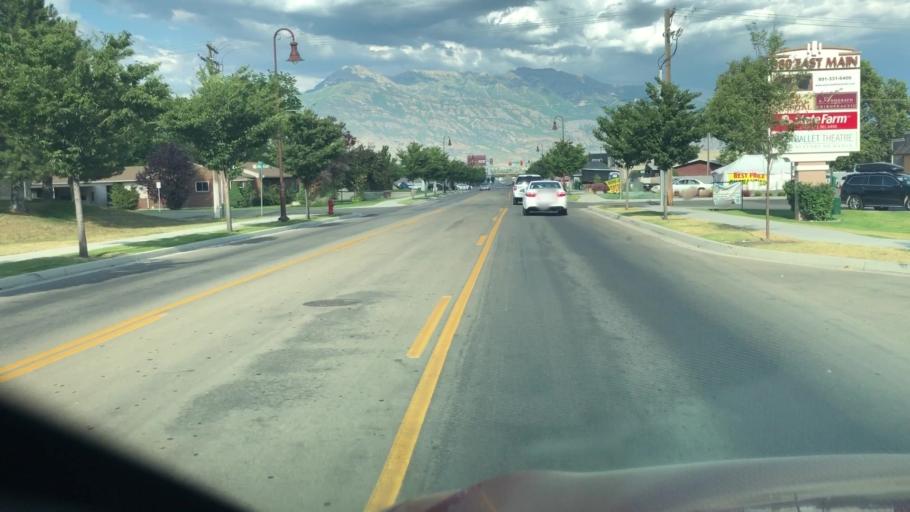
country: US
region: Utah
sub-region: Utah County
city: Lehi
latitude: 40.3880
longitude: -111.8435
